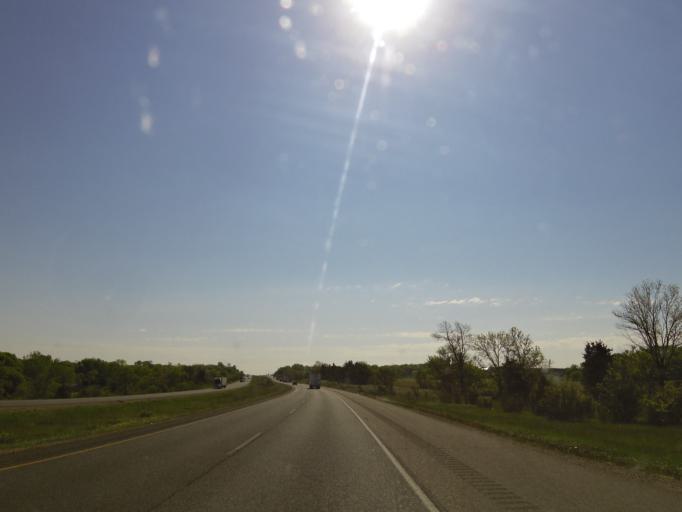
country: US
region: Wisconsin
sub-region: Saint Croix County
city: Roberts
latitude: 44.9637
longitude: -92.6511
